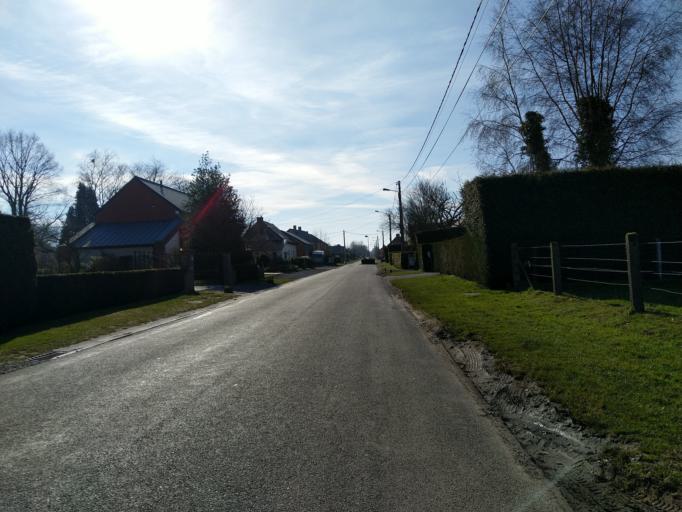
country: BE
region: Wallonia
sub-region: Province du Hainaut
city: Jurbise
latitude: 50.5191
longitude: 3.9619
